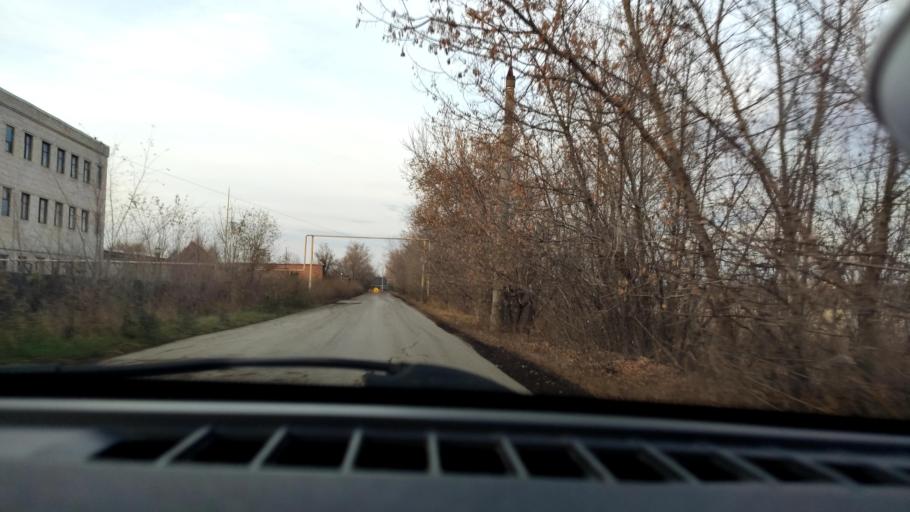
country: RU
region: Samara
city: Samara
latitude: 53.1352
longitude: 50.1364
